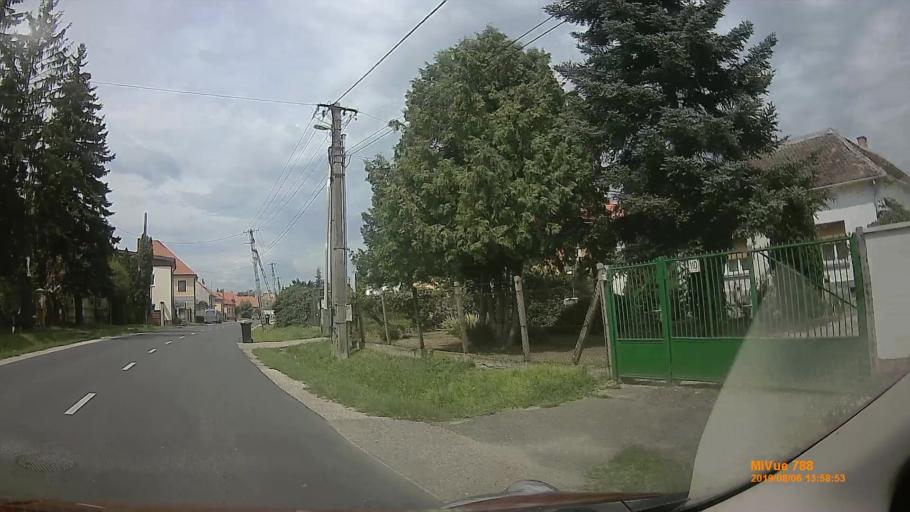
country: HU
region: Vas
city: Gencsapati
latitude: 47.2574
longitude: 16.6031
